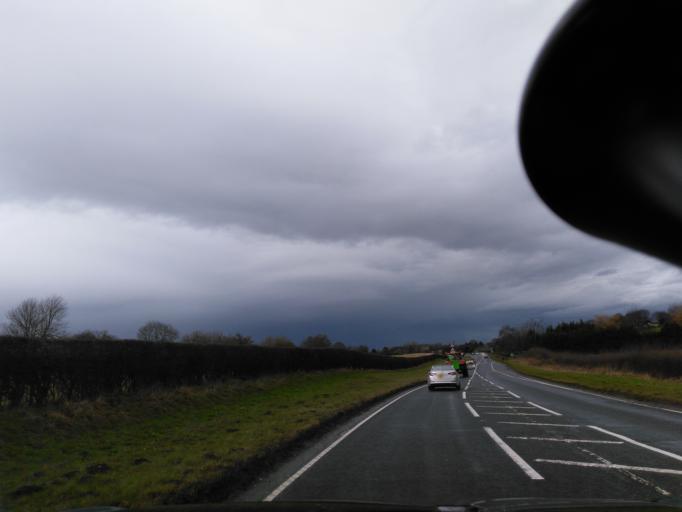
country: GB
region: England
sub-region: North Yorkshire
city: Ripon
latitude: 54.0703
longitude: -1.5374
